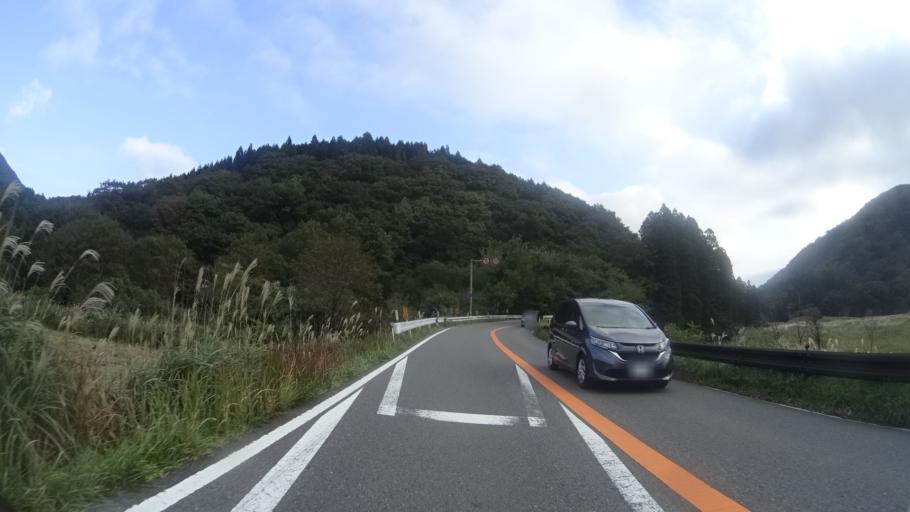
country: JP
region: Oita
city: Beppu
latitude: 33.2738
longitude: 131.4160
